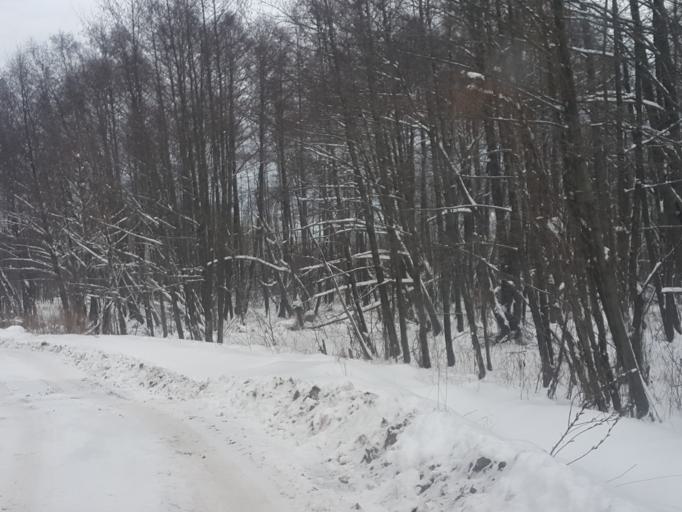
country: RU
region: Tambov
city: Platonovka
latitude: 52.8932
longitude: 41.8456
